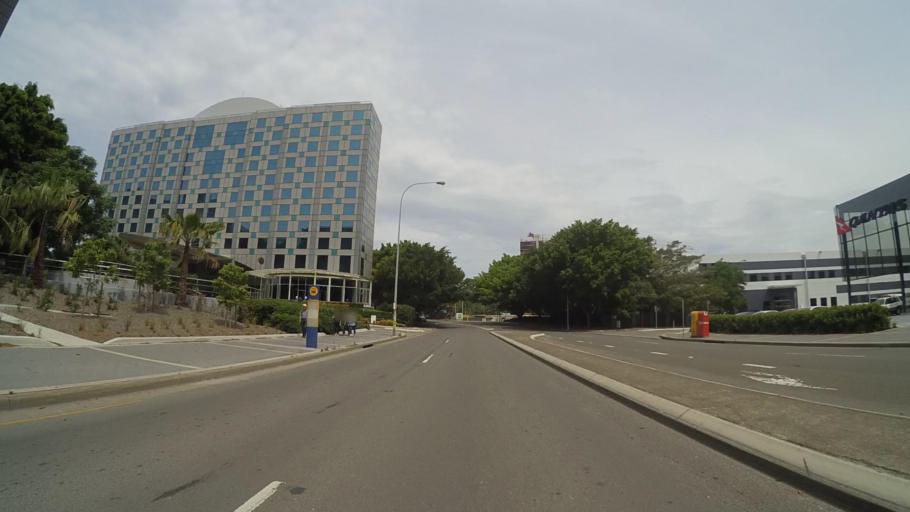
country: AU
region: New South Wales
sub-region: Botany Bay
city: Mascot
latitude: -33.9255
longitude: 151.1873
